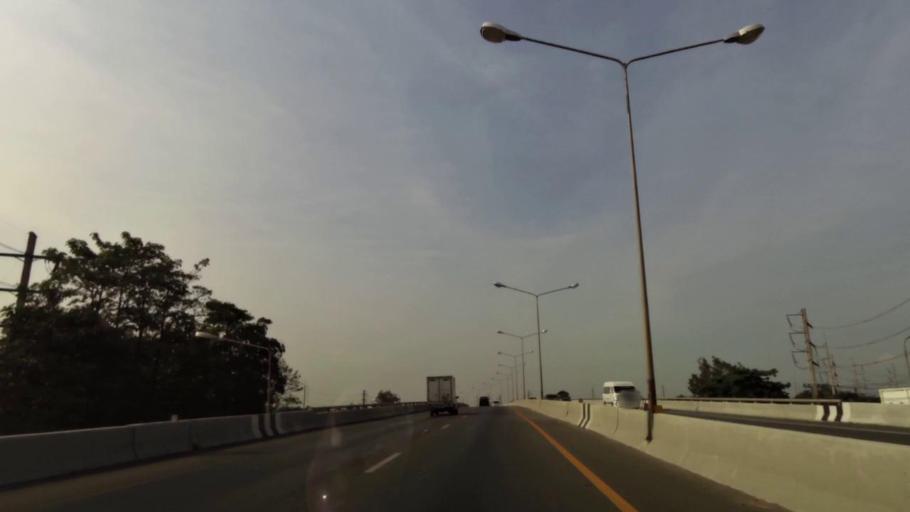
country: TH
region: Chon Buri
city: Ban Bueng
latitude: 13.2291
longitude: 101.2295
